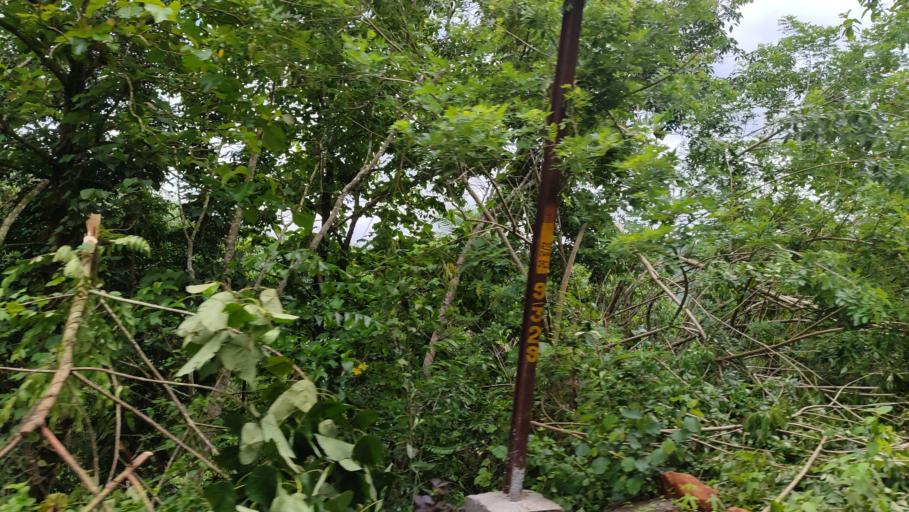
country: IN
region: Kerala
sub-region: Kasaragod District
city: Nileshwar
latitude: 12.2851
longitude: 75.2660
